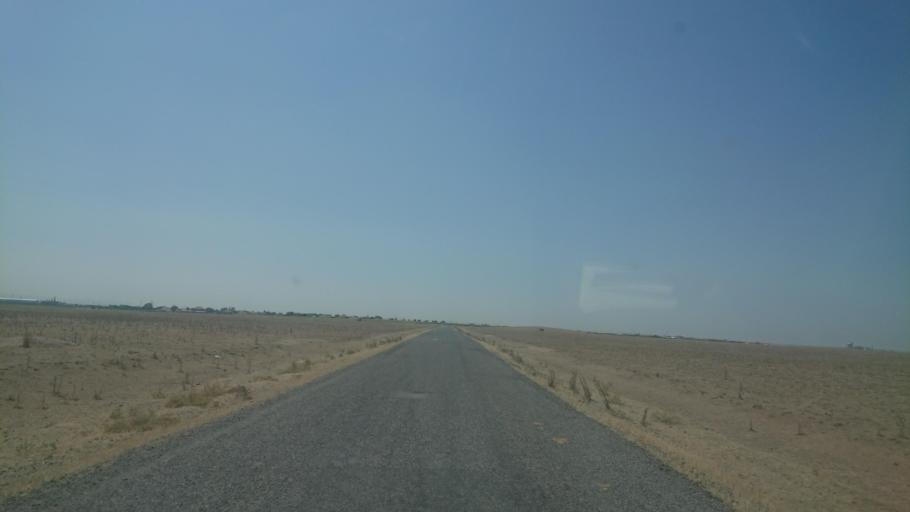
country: TR
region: Aksaray
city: Yesilova
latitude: 38.3028
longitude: 33.7324
